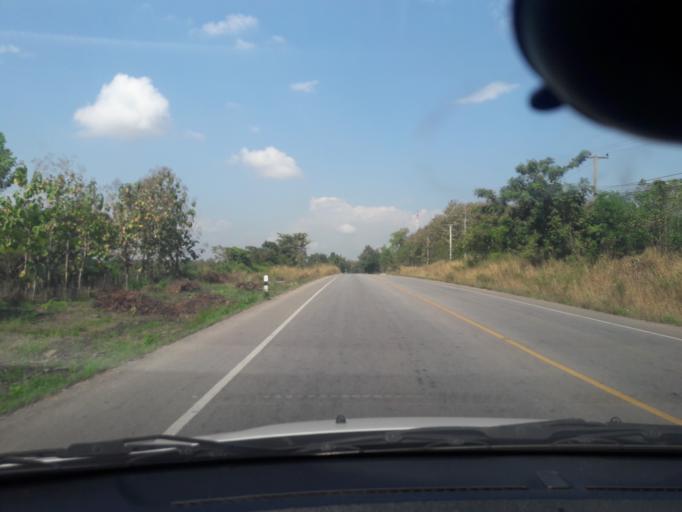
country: TH
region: Lampang
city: Mae Tha
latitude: 18.1944
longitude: 99.5165
